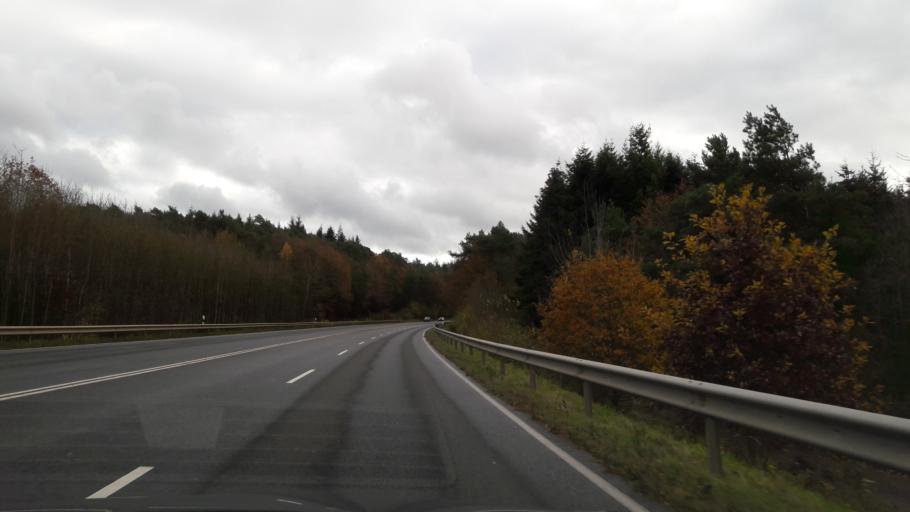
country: DE
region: Rheinland-Pfalz
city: Mertesdorf
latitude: 49.7819
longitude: 6.7455
